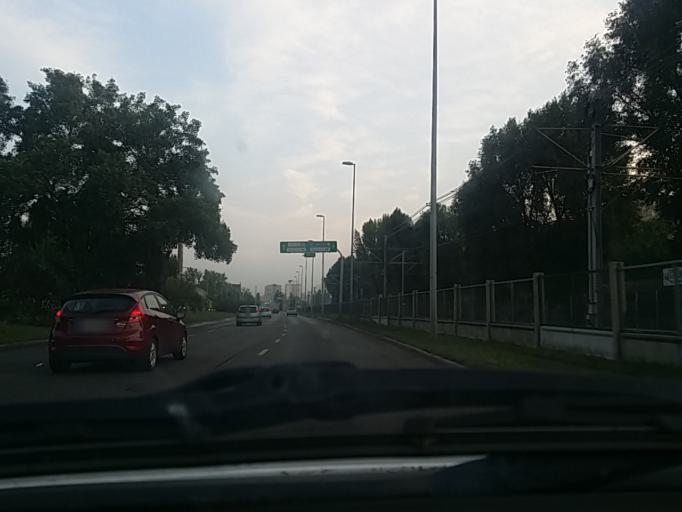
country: HU
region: Budapest
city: Budapest III. keruelet
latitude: 47.5605
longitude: 19.0470
